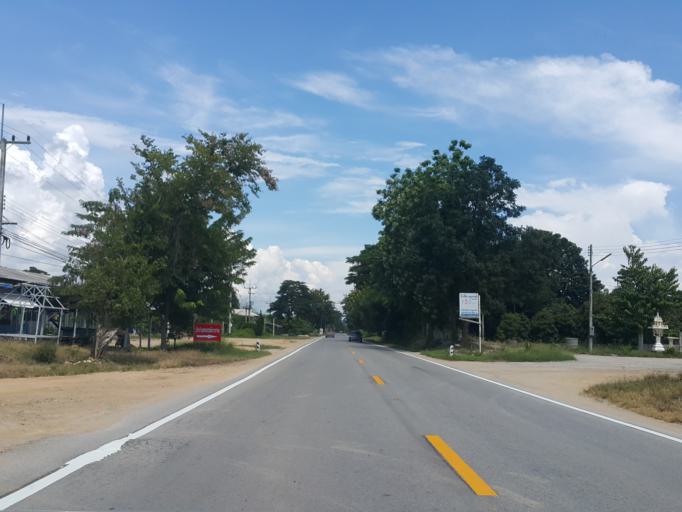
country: TH
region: Chiang Mai
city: Phrao
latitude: 19.2445
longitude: 99.1851
